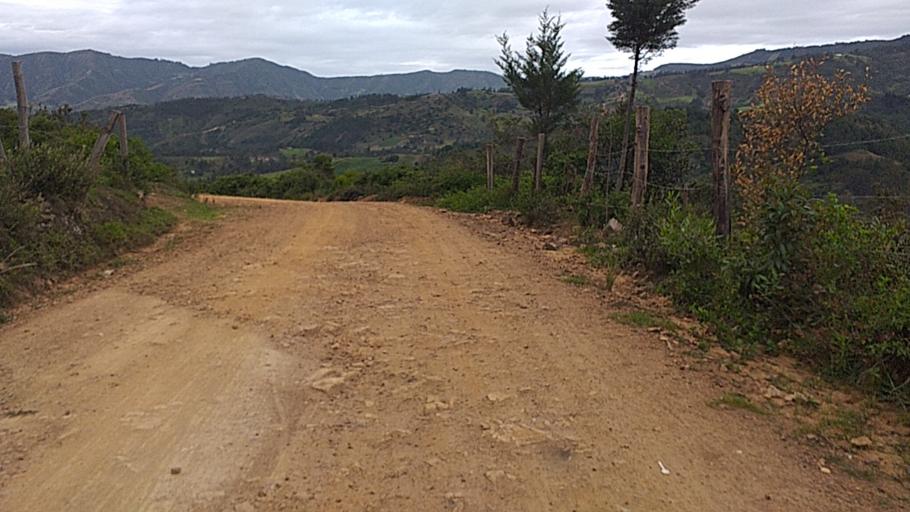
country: CO
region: Boyaca
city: Floresta
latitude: 5.8819
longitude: -72.9109
